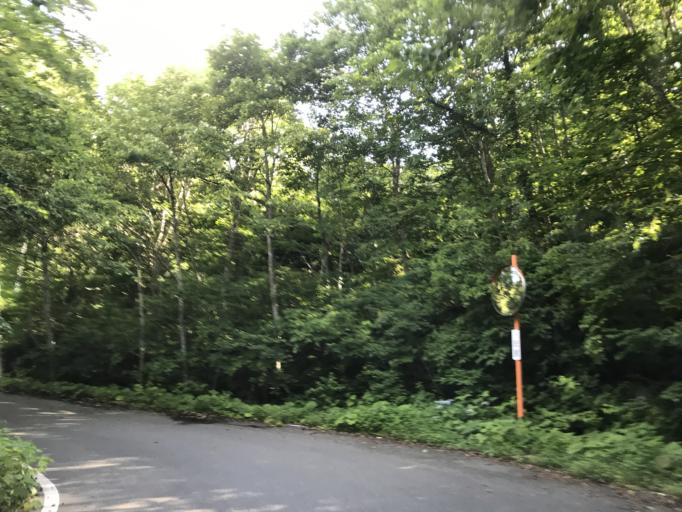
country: JP
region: Iwate
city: Ichinoseki
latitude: 38.9160
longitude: 140.8284
